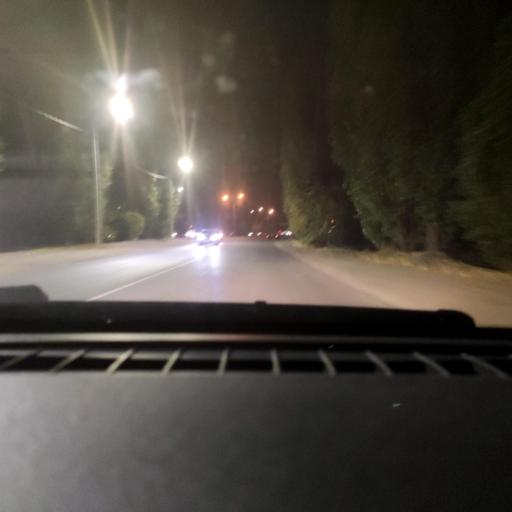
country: RU
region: Voronezj
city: Maslovka
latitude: 51.6240
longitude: 39.2609
